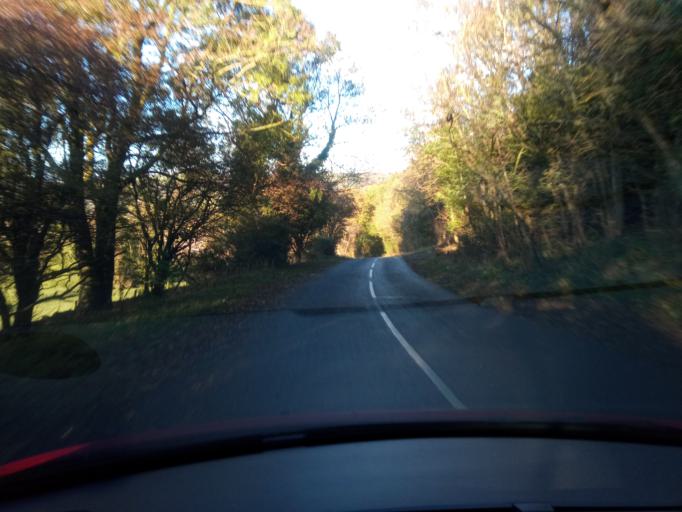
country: GB
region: England
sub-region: County Durham
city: Wolsingham
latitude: 54.7223
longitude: -1.8887
